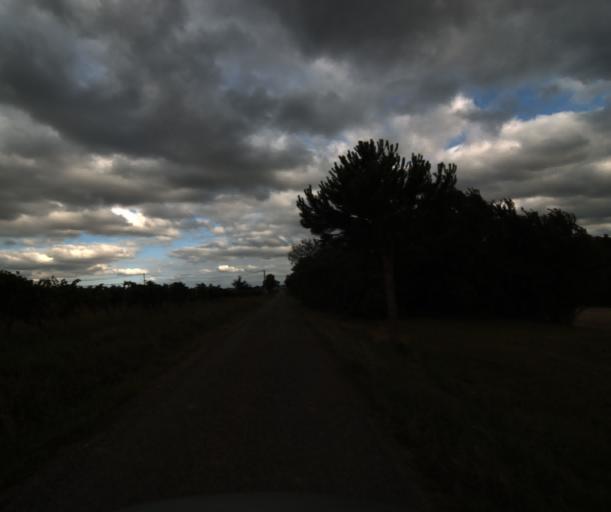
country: FR
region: Midi-Pyrenees
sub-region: Departement de la Haute-Garonne
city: Le Fauga
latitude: 43.3907
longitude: 1.3222
